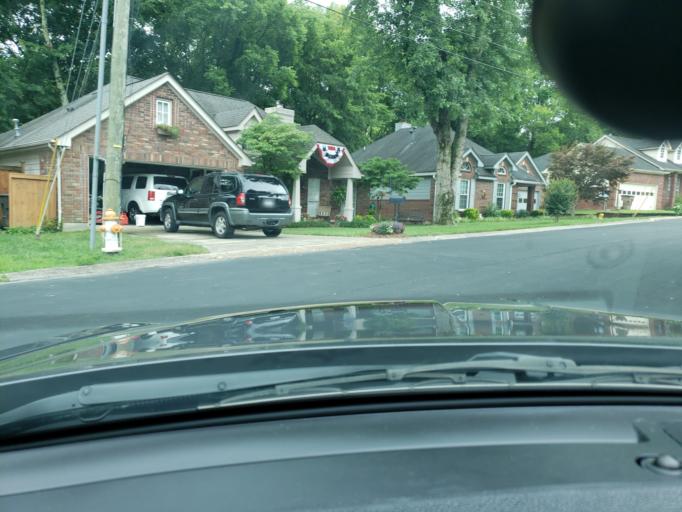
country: US
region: Tennessee
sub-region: Williamson County
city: Nolensville
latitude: 36.0360
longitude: -86.6775
